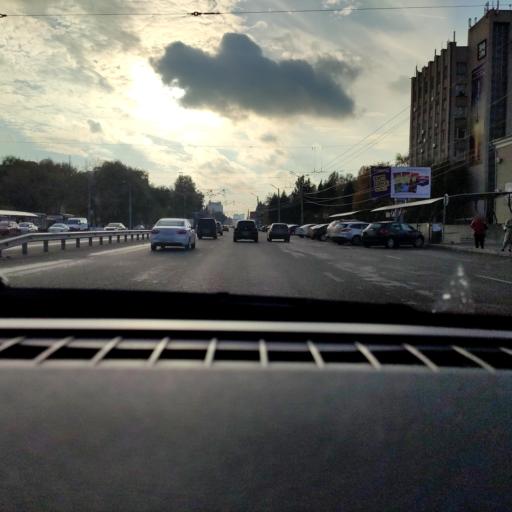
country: RU
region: Voronezj
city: Voronezh
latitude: 51.6534
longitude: 39.1711
